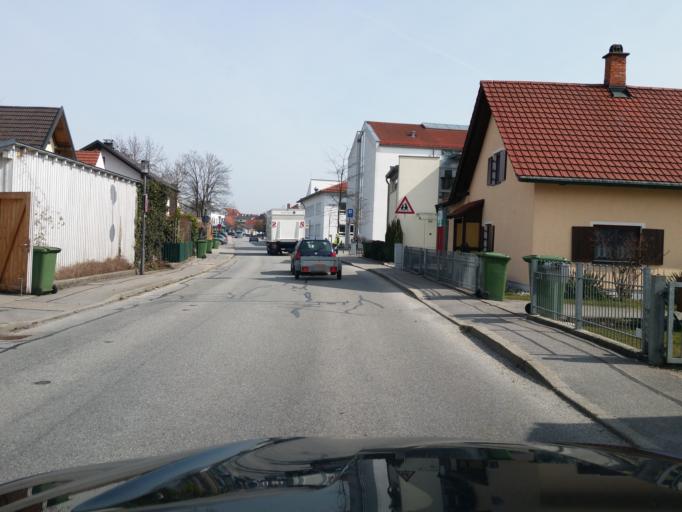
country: DE
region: Bavaria
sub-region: Lower Bavaria
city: Tiefenbach
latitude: 48.5542
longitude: 12.1065
